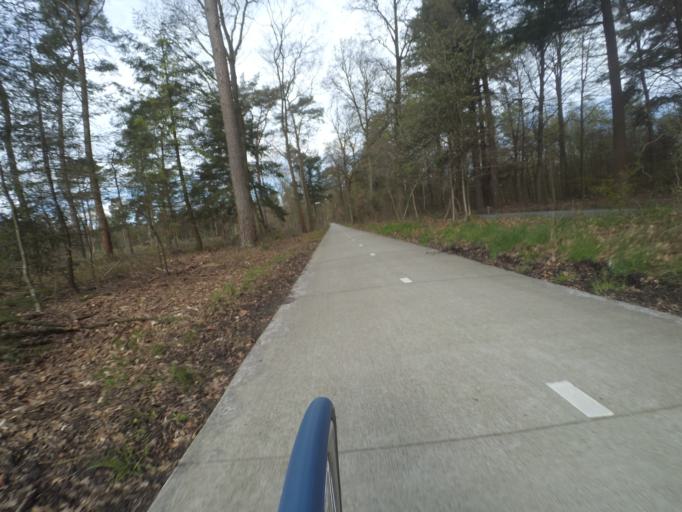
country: NL
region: Gelderland
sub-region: Gemeente Nunspeet
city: Nunspeet
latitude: 52.3394
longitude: 5.7958
